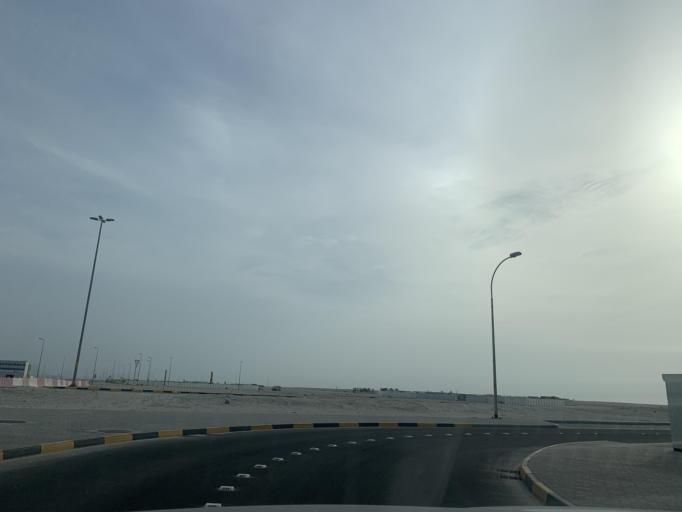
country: BH
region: Muharraq
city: Al Muharraq
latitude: 26.3134
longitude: 50.6209
